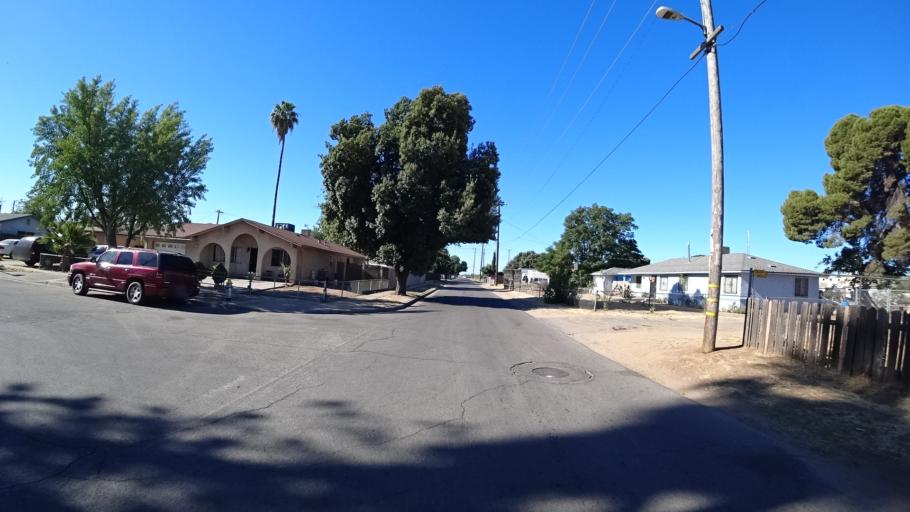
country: US
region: California
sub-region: Fresno County
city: West Park
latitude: 36.7231
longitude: -119.8267
